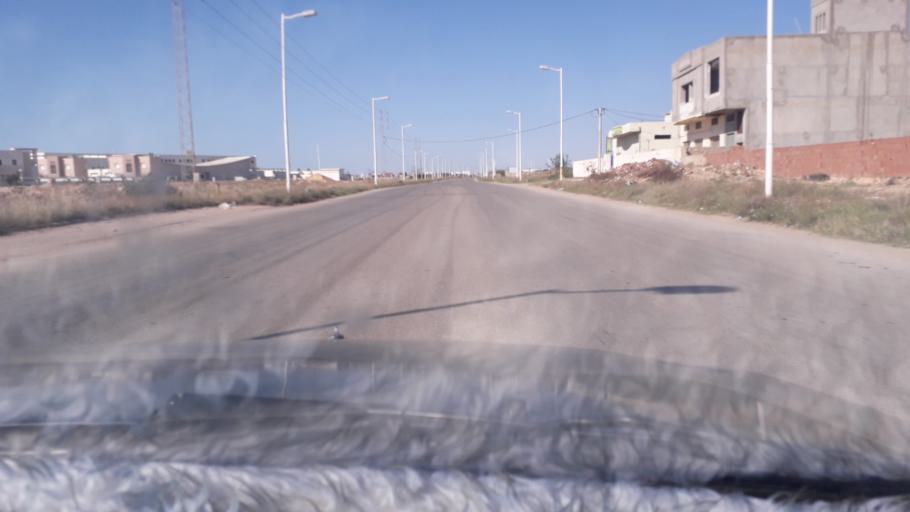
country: TN
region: Safaqis
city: Al Qarmadah
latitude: 34.8414
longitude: 10.7545
